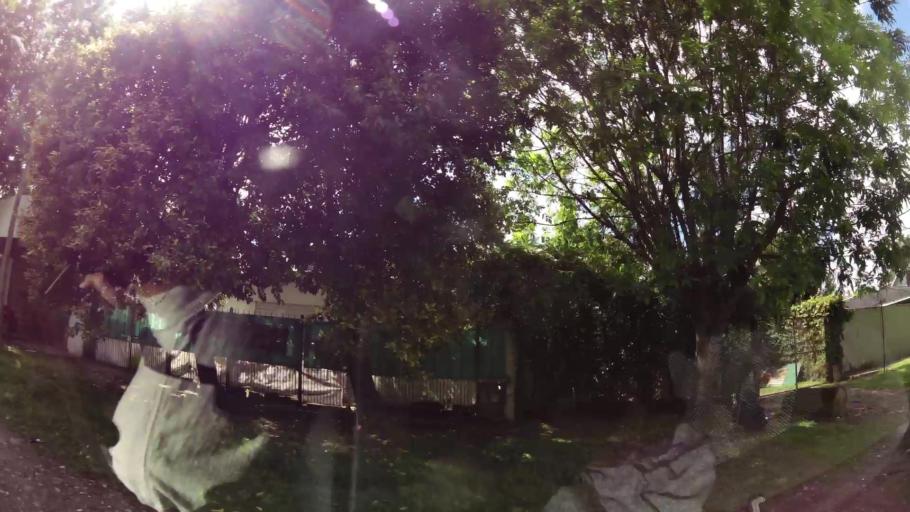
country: AR
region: Buenos Aires
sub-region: Partido de Quilmes
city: Quilmes
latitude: -34.8348
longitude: -58.1717
